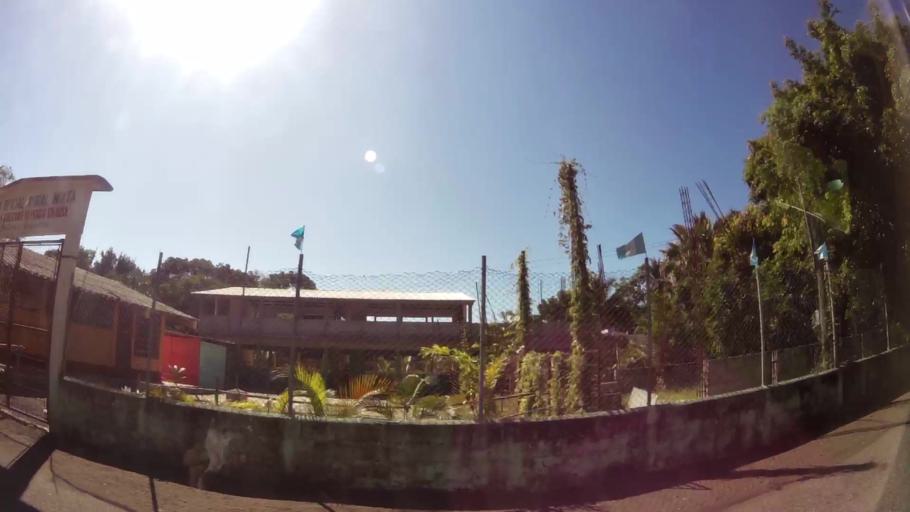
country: GT
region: Santa Rosa
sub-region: Municipio de Taxisco
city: Taxisco
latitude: 13.9074
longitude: -90.5161
